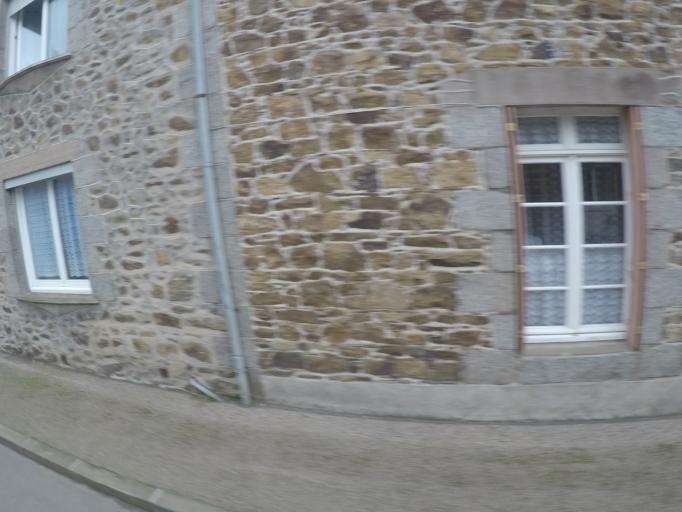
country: FR
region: Brittany
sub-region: Departement des Cotes-d'Armor
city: Pommerit-le-Vicomte
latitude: 48.6414
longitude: -3.0491
